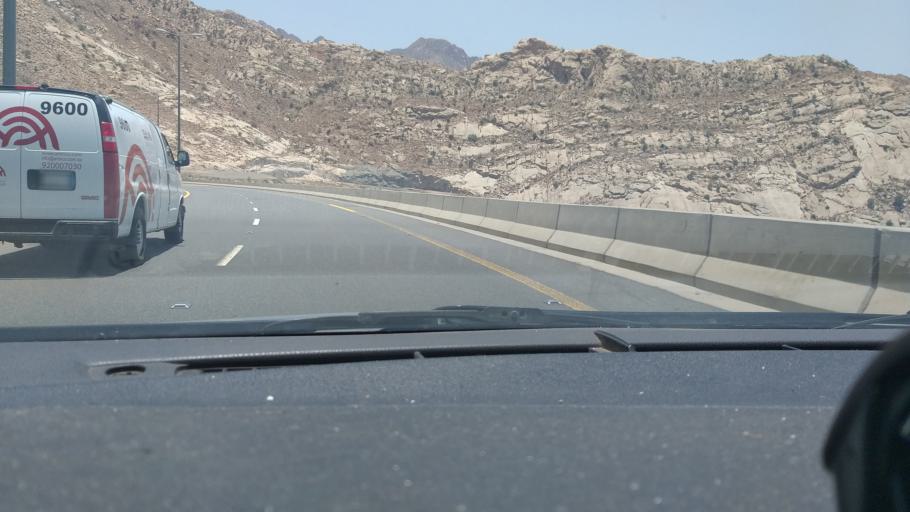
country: SA
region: Makkah
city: Al Hada
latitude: 21.3432
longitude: 40.2561
